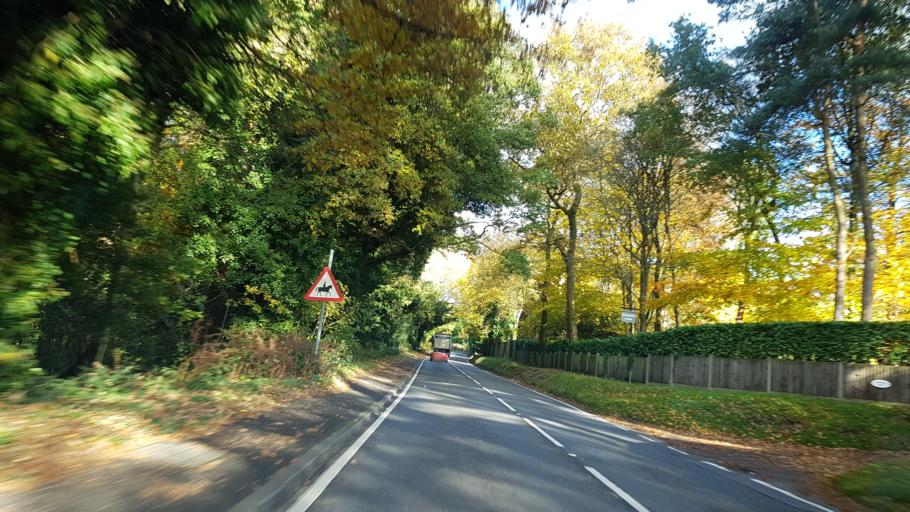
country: GB
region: England
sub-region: Surrey
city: Hindhead
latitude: 51.1079
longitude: -0.7323
